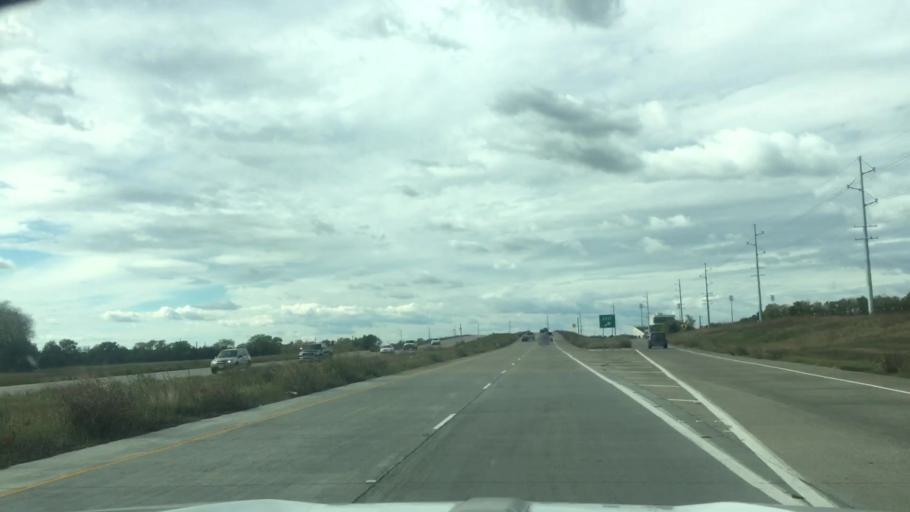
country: US
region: Texas
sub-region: Denton County
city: Denton
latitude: 33.2557
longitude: -97.1052
